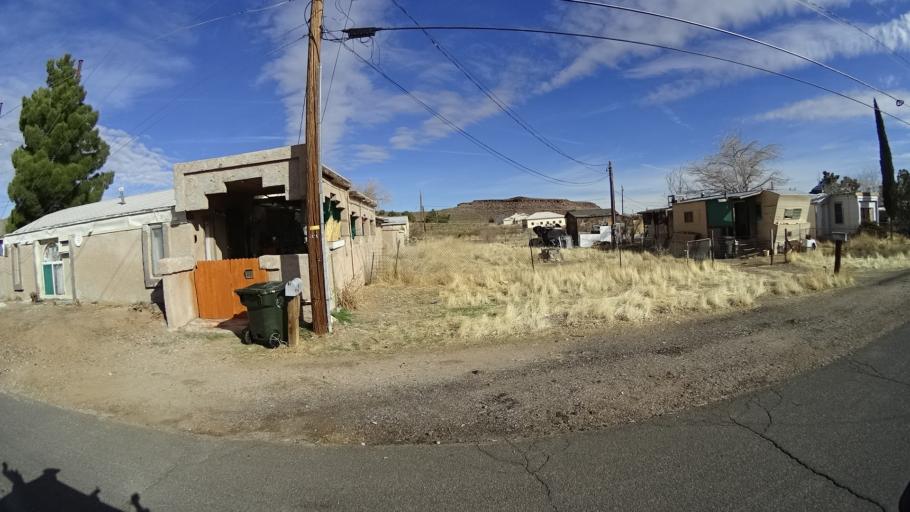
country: US
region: Arizona
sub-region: Mohave County
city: Kingman
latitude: 35.2178
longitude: -114.0530
